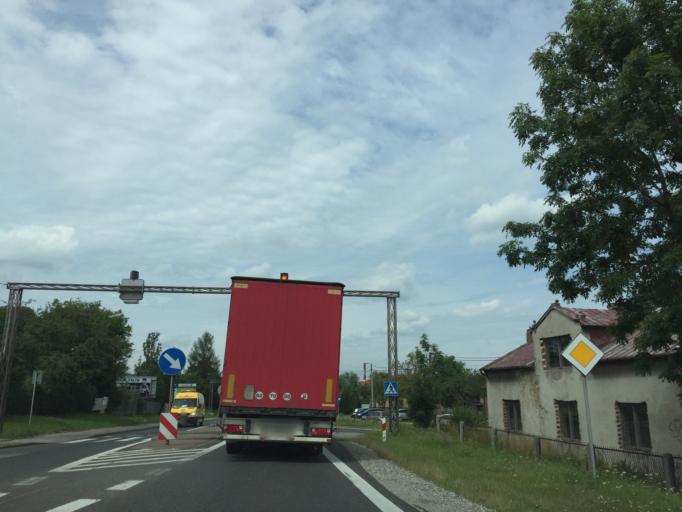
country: PL
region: Lesser Poland Voivodeship
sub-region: Powiat olkuski
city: Osiek
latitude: 50.2668
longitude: 19.6136
